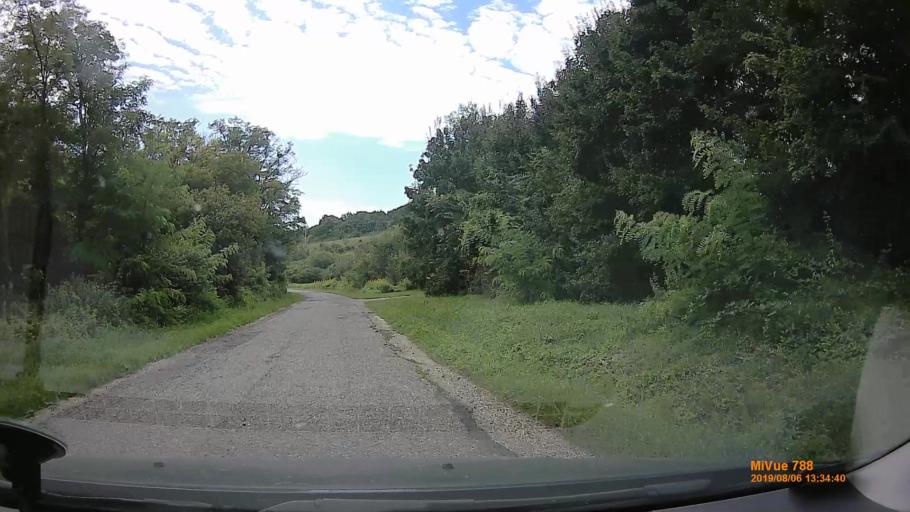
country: HU
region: Zala
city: Zalakomar
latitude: 46.5760
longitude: 17.1131
